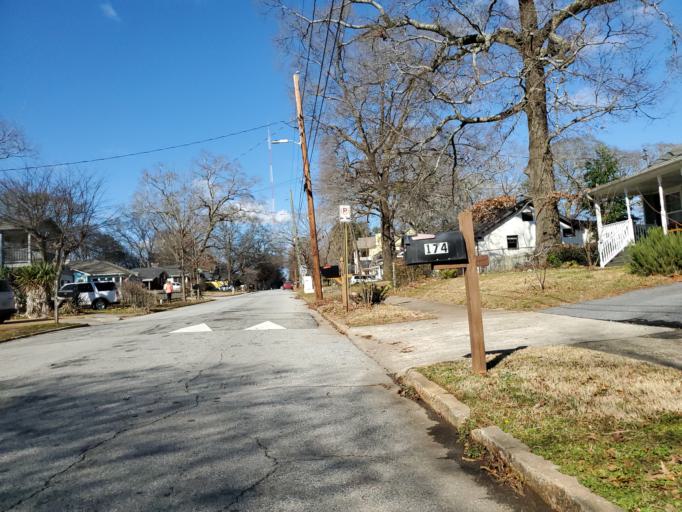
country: US
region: Georgia
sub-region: DeKalb County
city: Druid Hills
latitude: 33.7486
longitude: -84.3318
